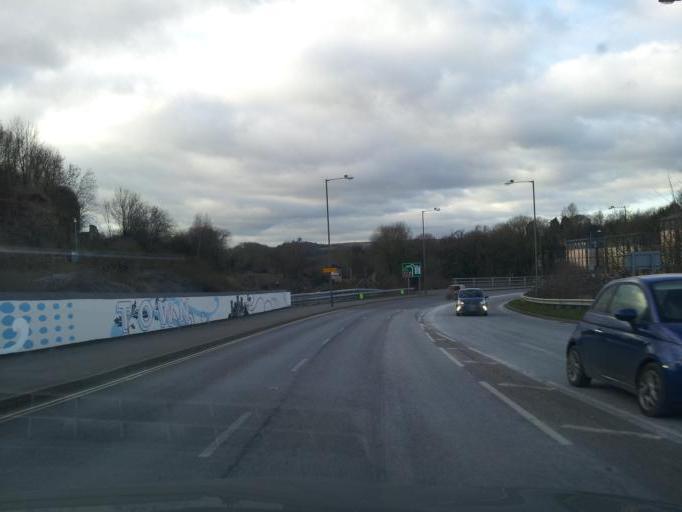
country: GB
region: England
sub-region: Derbyshire
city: Matlock
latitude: 53.1402
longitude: -1.5637
